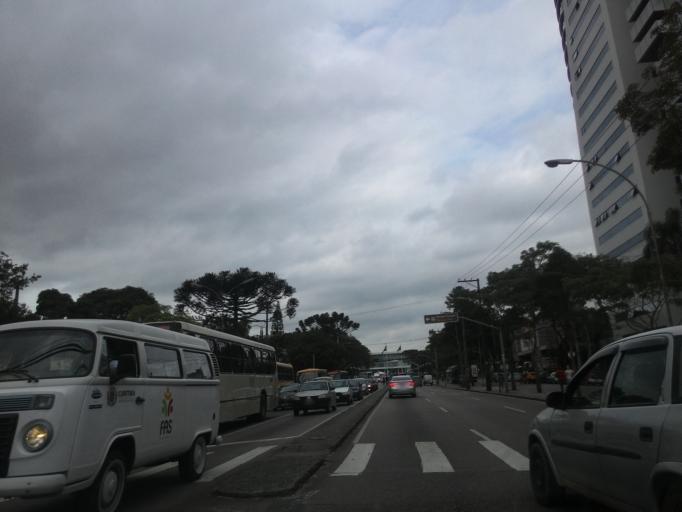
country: BR
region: Parana
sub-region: Curitiba
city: Curitiba
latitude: -25.4188
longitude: -49.2688
